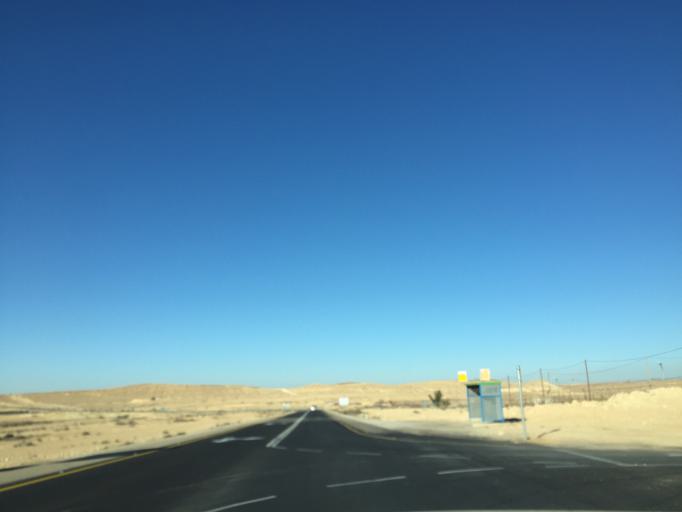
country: IL
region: Southern District
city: Mitzpe Ramon
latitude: 30.6525
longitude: 34.8102
